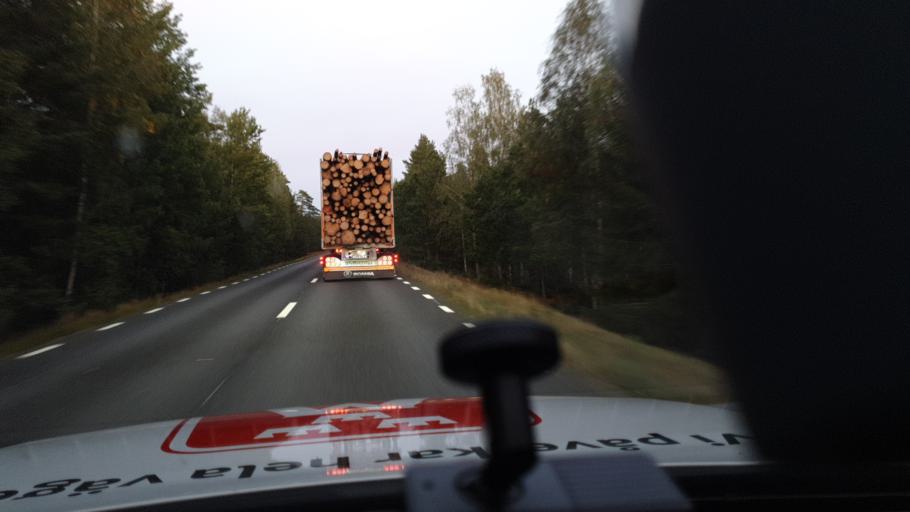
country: SE
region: Kalmar
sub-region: Monsteras Kommun
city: Blomstermala
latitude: 57.1233
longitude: 16.2257
